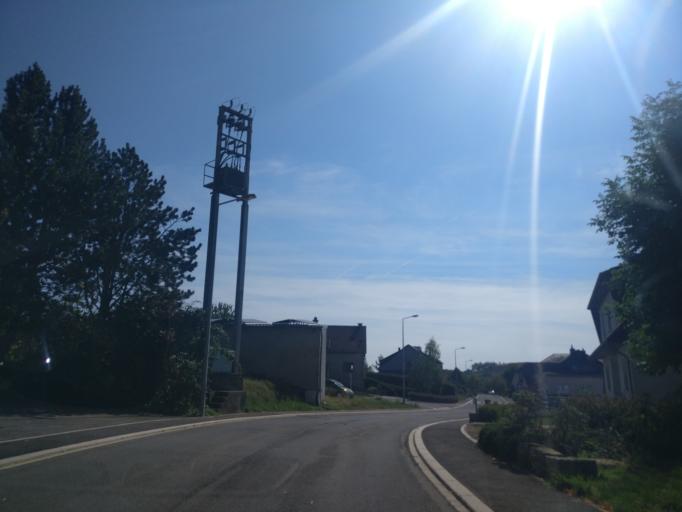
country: DE
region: Rheinland-Pfalz
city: Wellen
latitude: 49.6490
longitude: 6.3998
